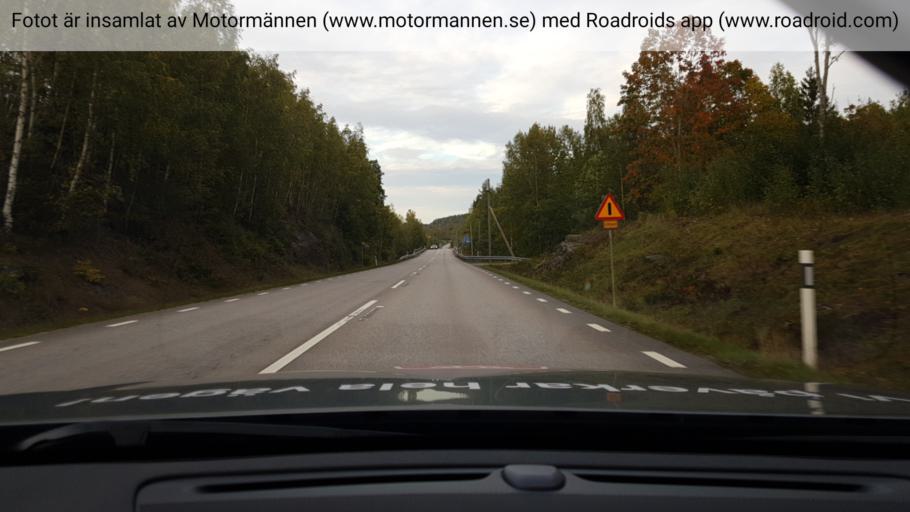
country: SE
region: Vaestra Goetaland
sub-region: Bengtsfors Kommun
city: Bengtsfors
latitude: 59.0213
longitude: 12.2726
